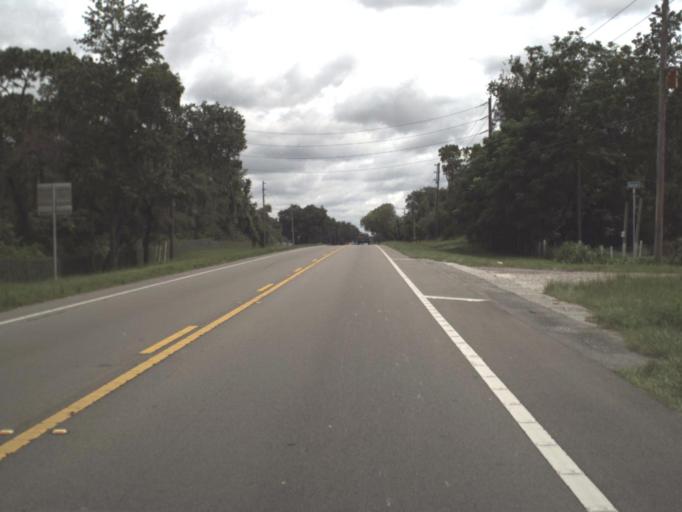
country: US
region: Florida
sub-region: Hernando County
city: Masaryktown
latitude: 28.4097
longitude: -82.4752
